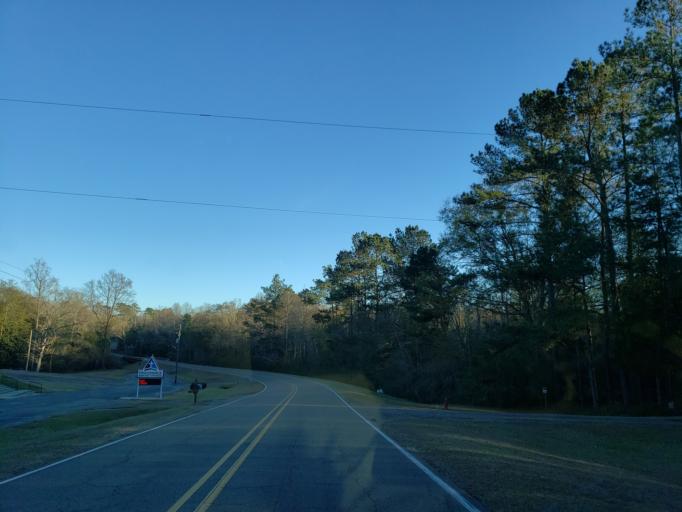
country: US
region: Mississippi
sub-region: Forrest County
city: Rawls Springs
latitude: 31.4288
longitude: -89.3586
